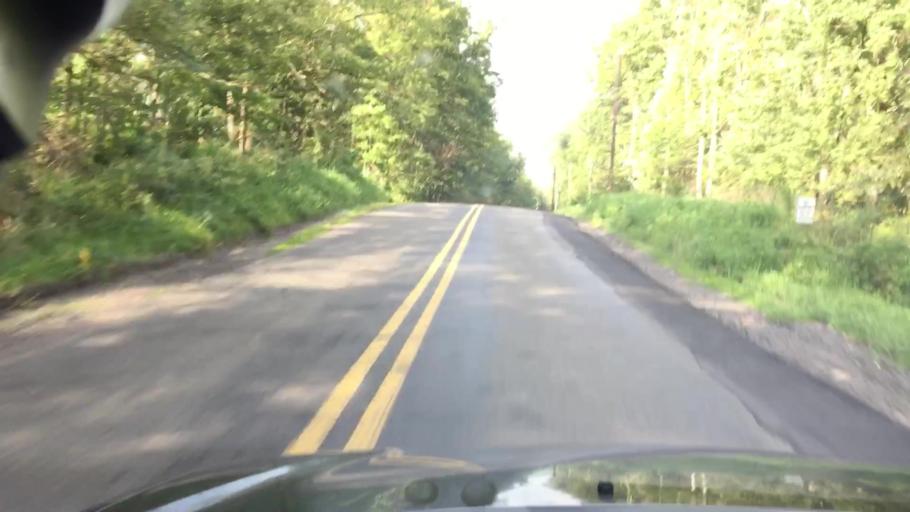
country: US
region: Pennsylvania
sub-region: Luzerne County
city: Harleigh
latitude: 41.0372
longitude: -75.9799
